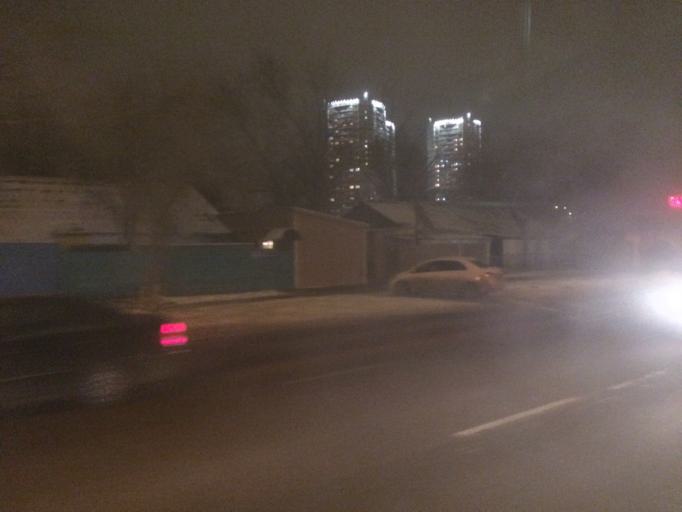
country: KZ
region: Astana Qalasy
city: Astana
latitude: 51.1631
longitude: 71.4622
